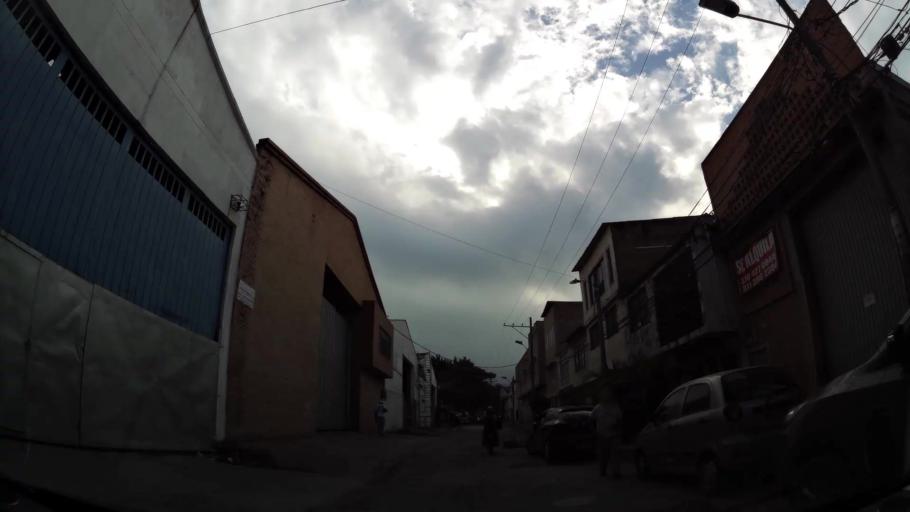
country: CO
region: Valle del Cauca
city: Cali
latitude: 3.4650
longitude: -76.5097
